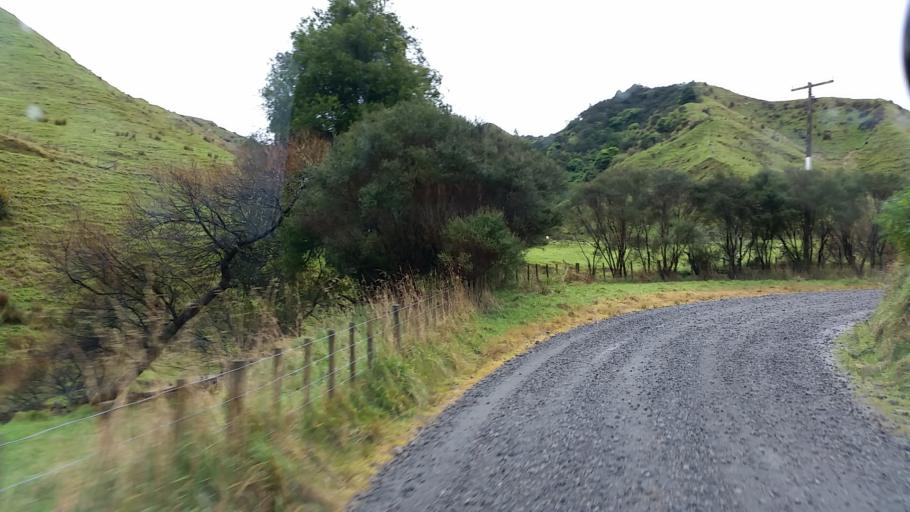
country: NZ
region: Taranaki
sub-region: South Taranaki District
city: Eltham
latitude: -39.4951
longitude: 174.4329
